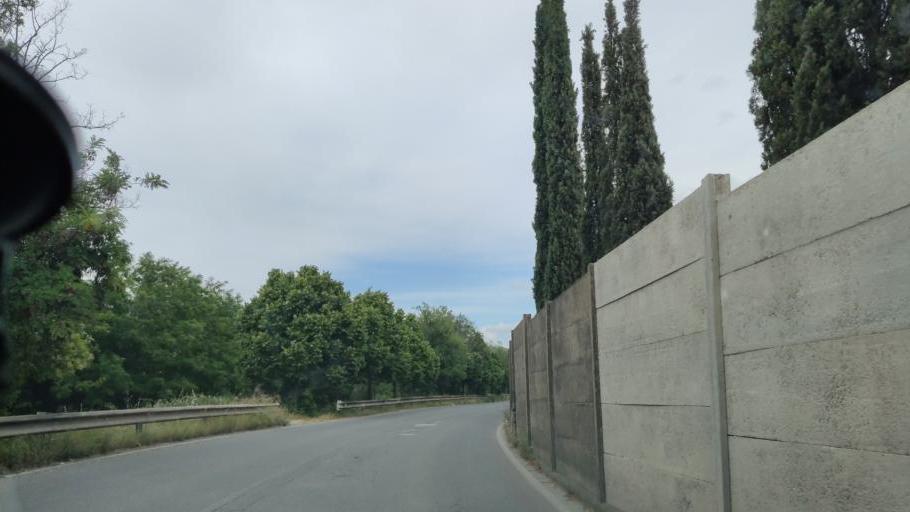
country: IT
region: Umbria
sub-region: Provincia di Terni
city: Terni
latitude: 42.5716
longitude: 12.6713
